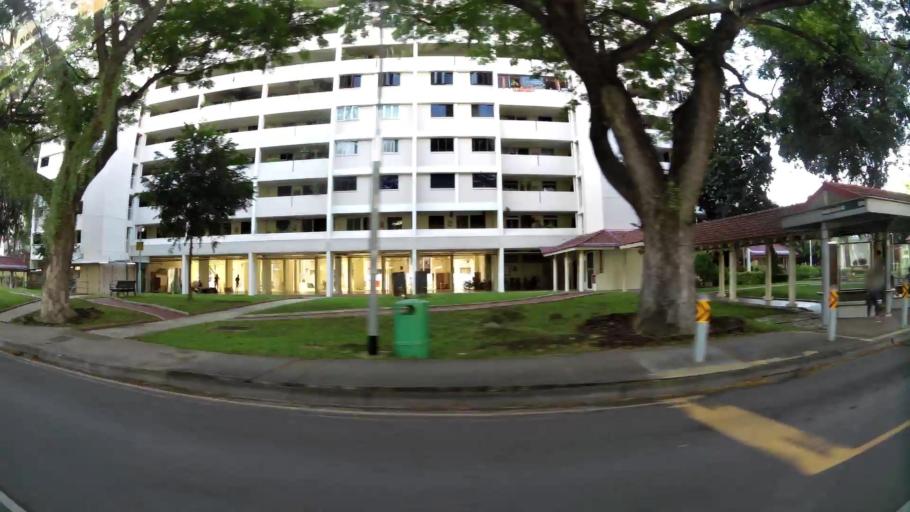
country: SG
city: Singapore
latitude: 1.3206
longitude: 103.9425
